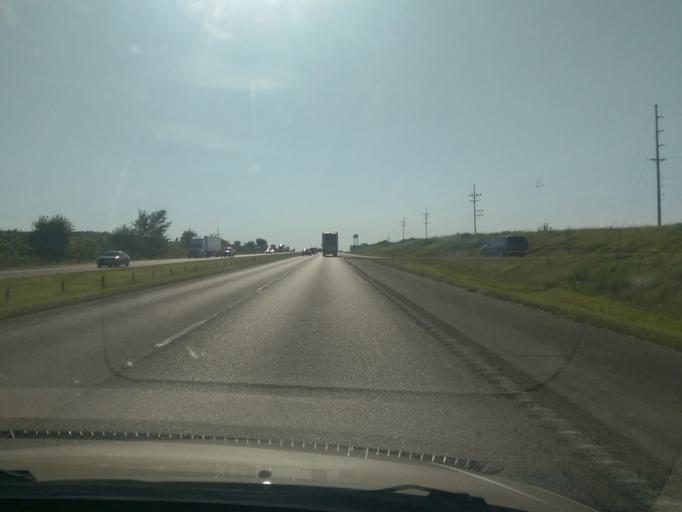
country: US
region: Missouri
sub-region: Lafayette County
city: Higginsville
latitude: 39.0028
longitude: -93.8107
